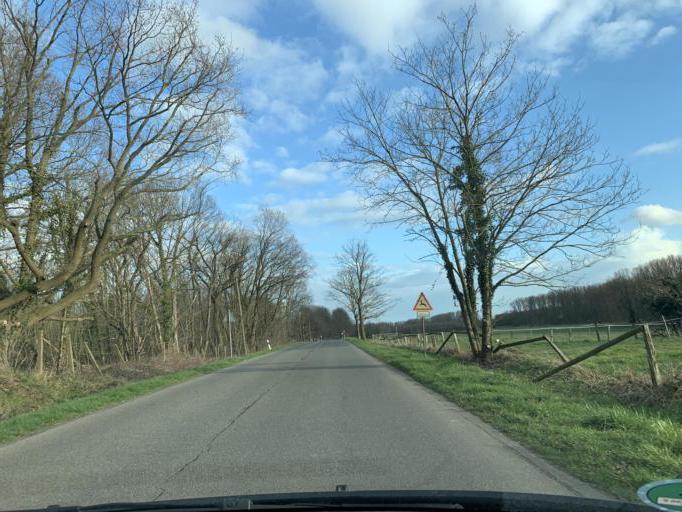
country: DE
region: North Rhine-Westphalia
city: Julich
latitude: 50.9179
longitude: 6.4150
